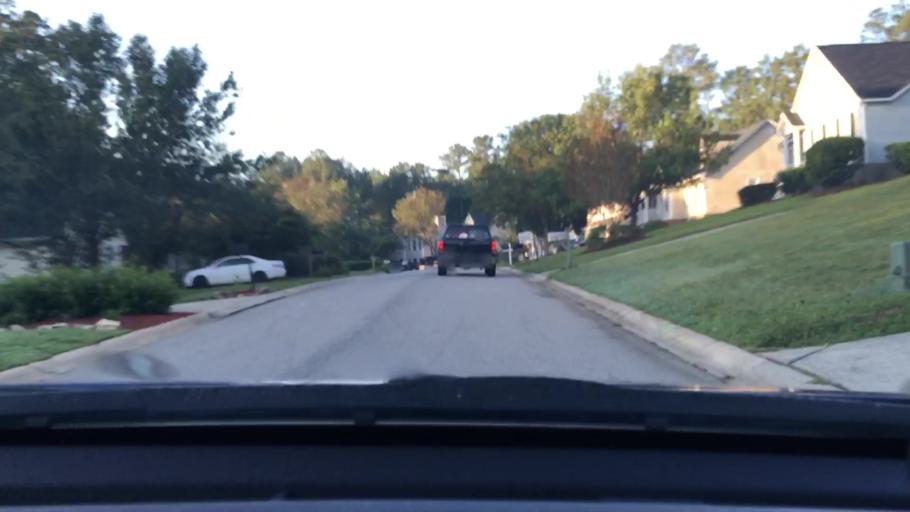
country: US
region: South Carolina
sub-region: Lexington County
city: Irmo
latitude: 34.1039
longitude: -81.1551
